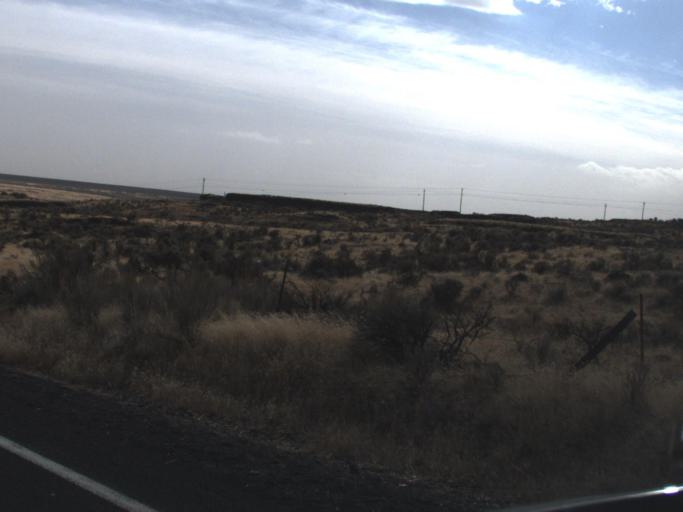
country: US
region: Washington
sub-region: Adams County
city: Ritzville
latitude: 47.4686
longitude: -118.7721
